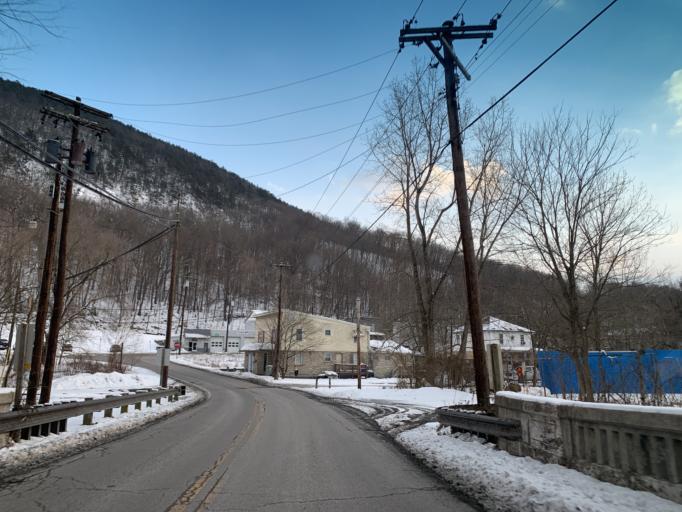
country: US
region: Maryland
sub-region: Allegany County
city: La Vale
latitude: 39.6702
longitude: -78.7934
